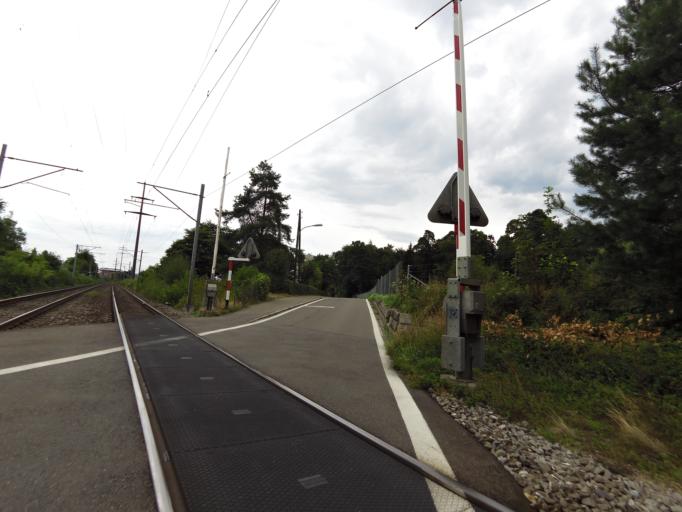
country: CH
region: Zurich
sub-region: Bezirk Zuerich
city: Zuerich (Kreis 11) / Affoltern
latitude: 47.4185
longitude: 8.5153
